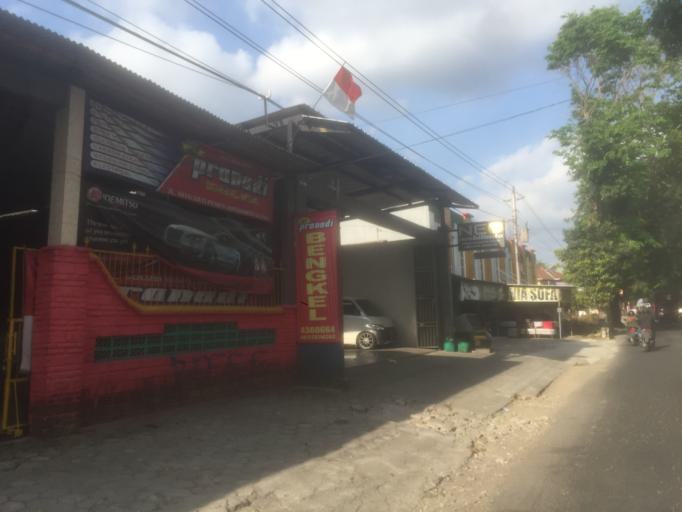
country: ID
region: Daerah Istimewa Yogyakarta
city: Melati
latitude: -7.7190
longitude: 110.3709
